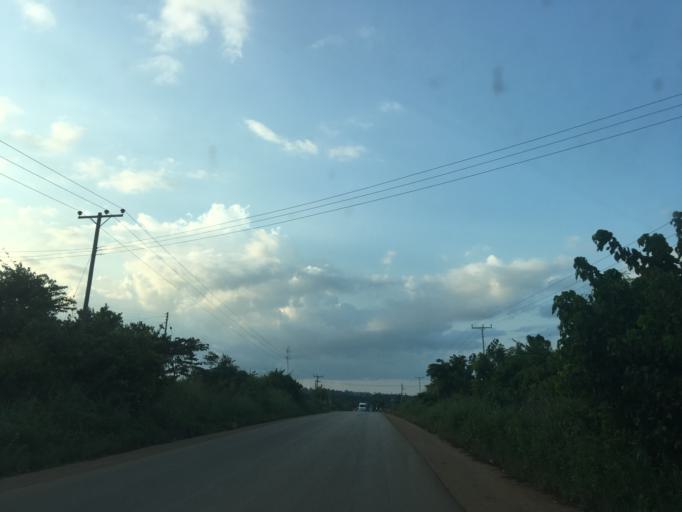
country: GH
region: Western
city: Bibiani
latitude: 6.6442
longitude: -2.4249
